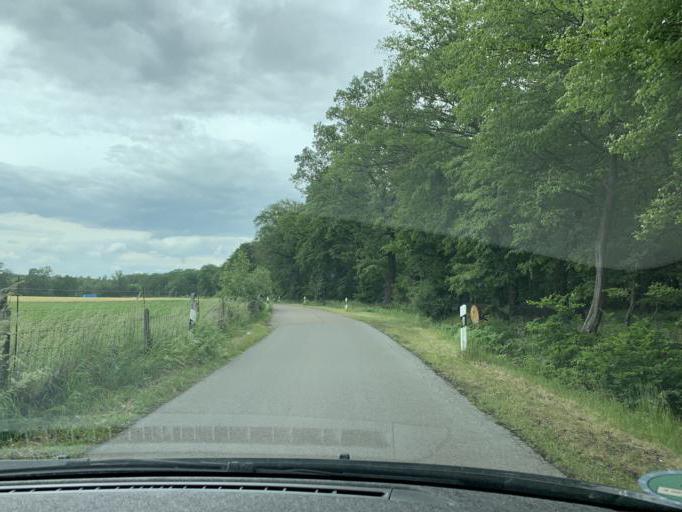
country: DE
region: North Rhine-Westphalia
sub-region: Regierungsbezirk Koln
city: Niederzier
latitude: 50.8764
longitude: 6.5136
